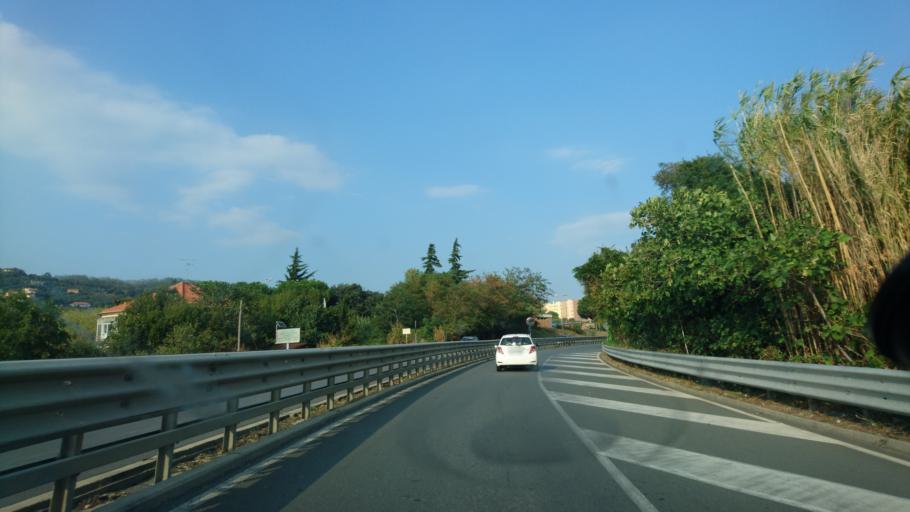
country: IT
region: Liguria
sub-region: Provincia di Savona
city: Valleggia
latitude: 44.2854
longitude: 8.4414
